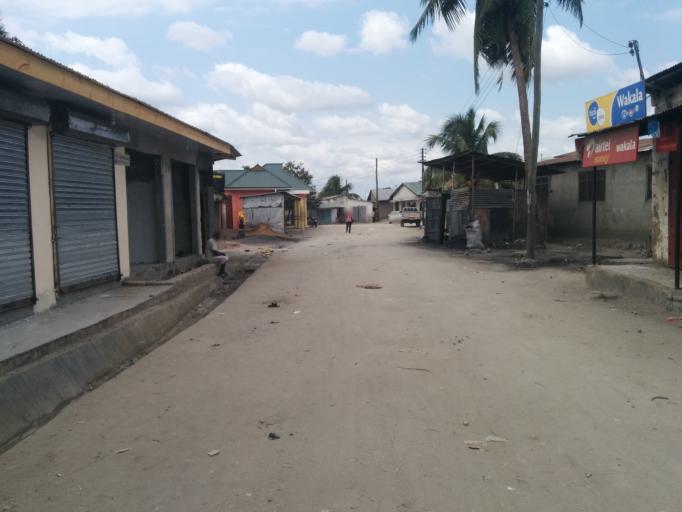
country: TZ
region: Dar es Salaam
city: Dar es Salaam
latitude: -6.8621
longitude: 39.2500
